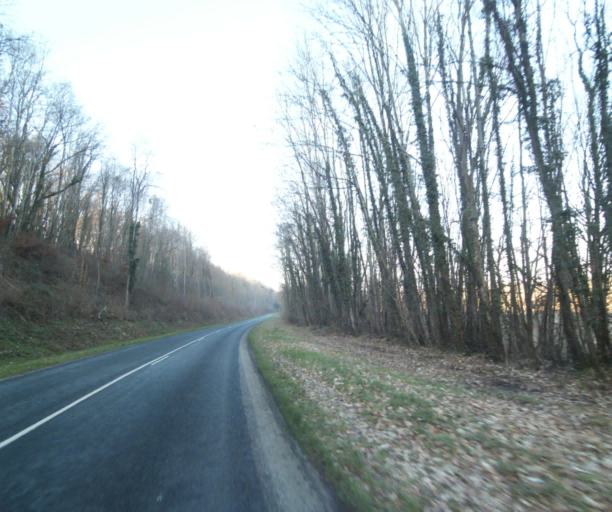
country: FR
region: Champagne-Ardenne
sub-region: Departement de la Haute-Marne
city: Bienville
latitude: 48.5715
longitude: 5.0374
